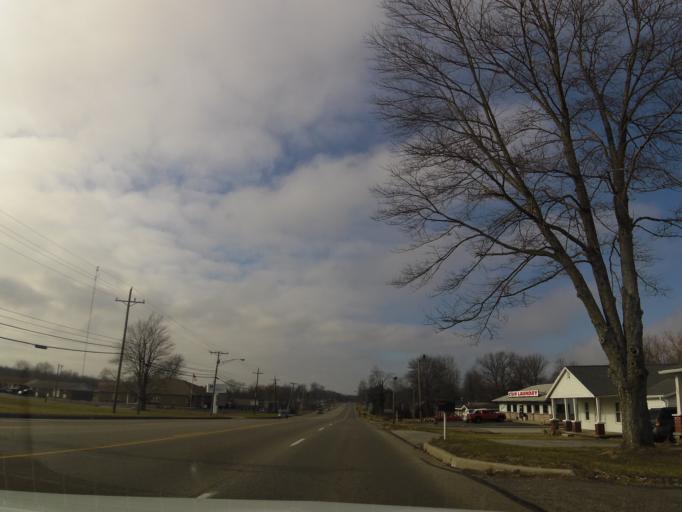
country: US
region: Indiana
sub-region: Jefferson County
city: North Madison
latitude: 38.7717
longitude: -85.4176
